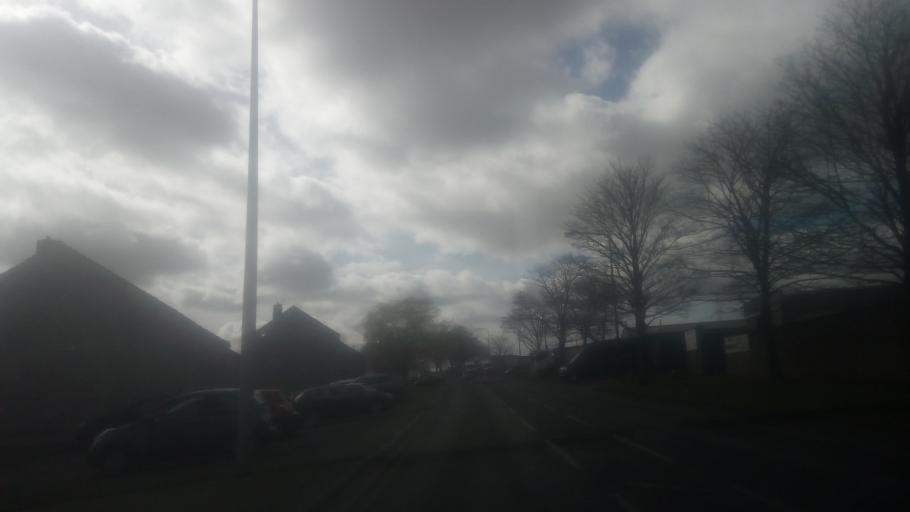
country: GB
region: Scotland
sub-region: East Lothian
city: Tranent
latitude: 55.9434
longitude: -2.9609
